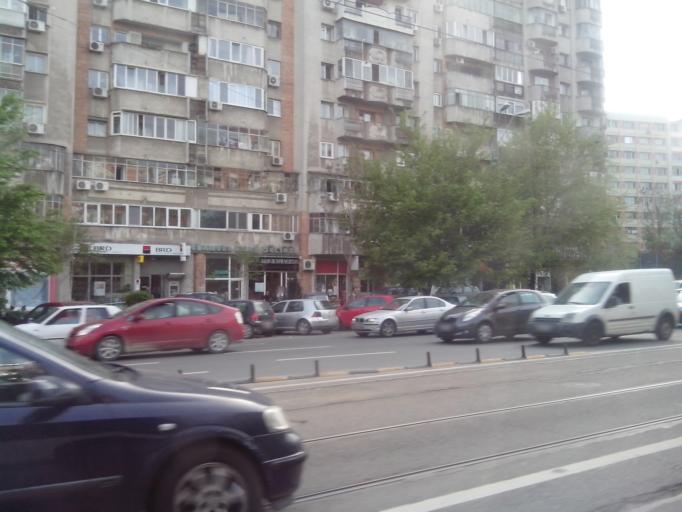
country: RO
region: Bucuresti
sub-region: Municipiul Bucuresti
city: Bucharest
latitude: 44.4420
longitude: 26.1322
